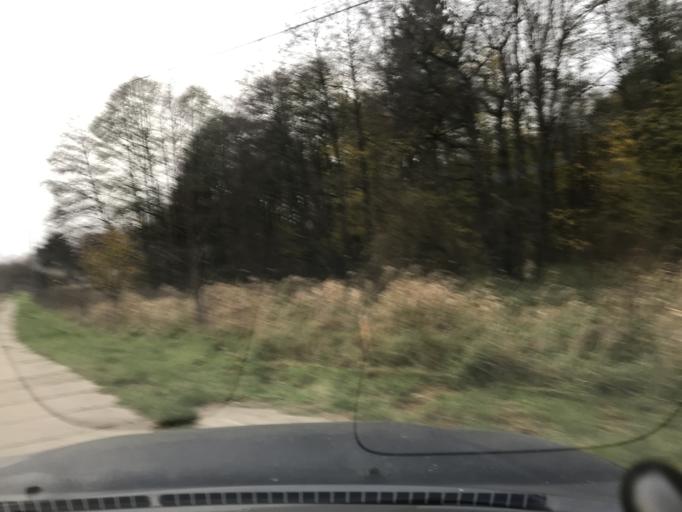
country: PL
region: Pomeranian Voivodeship
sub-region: Powiat slupski
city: Kobylnica
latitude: 54.4572
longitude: 16.8821
